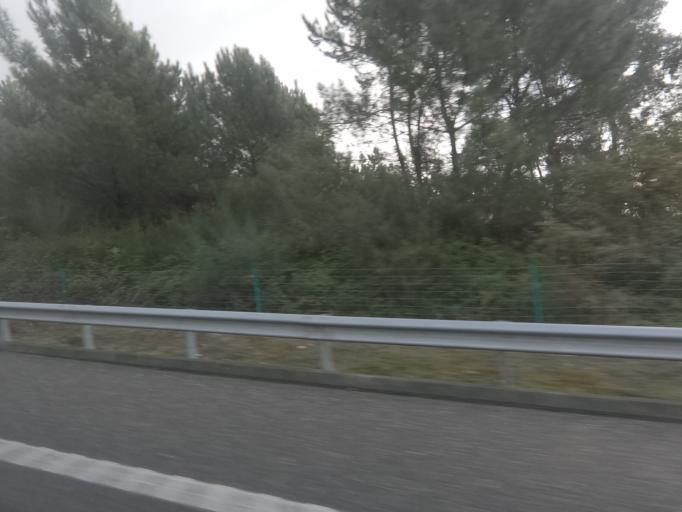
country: ES
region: Galicia
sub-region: Provincia de Pontevedra
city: Porrino
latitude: 42.1808
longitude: -8.6508
